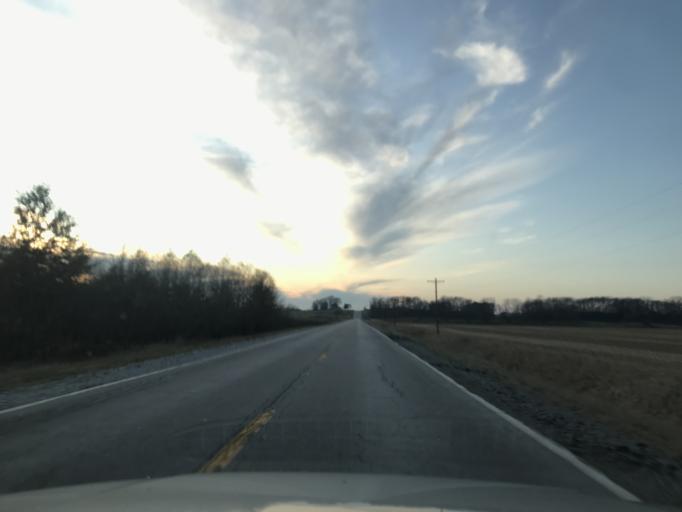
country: US
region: Illinois
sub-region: Henderson County
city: Oquawka
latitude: 41.0190
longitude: -90.8202
